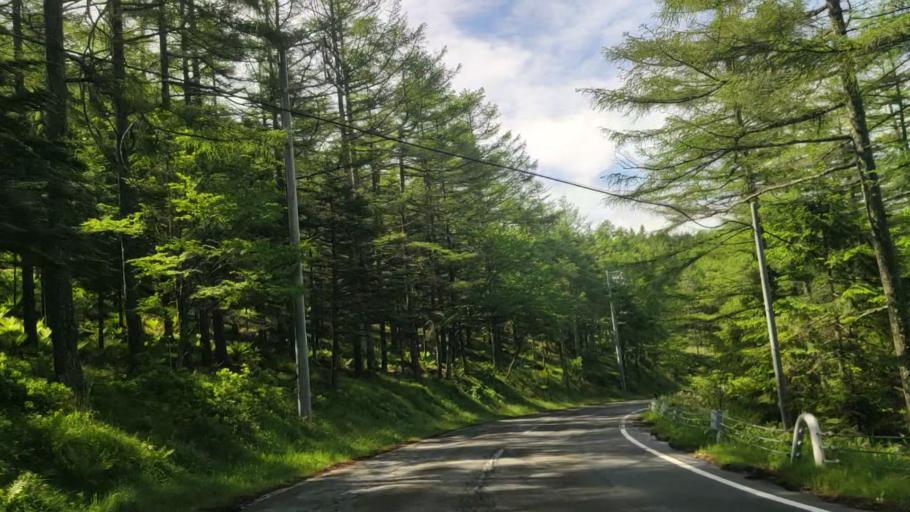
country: JP
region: Nagano
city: Suwa
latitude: 36.0966
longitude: 138.1516
